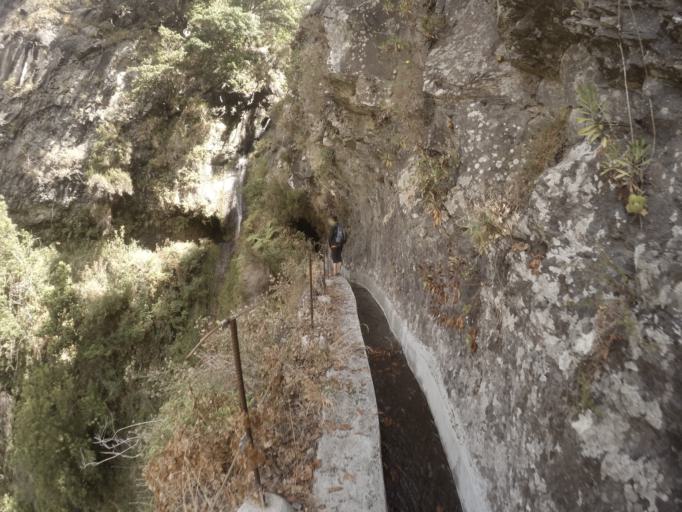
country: PT
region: Madeira
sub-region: Camara de Lobos
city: Curral das Freiras
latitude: 32.7020
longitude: -16.9635
